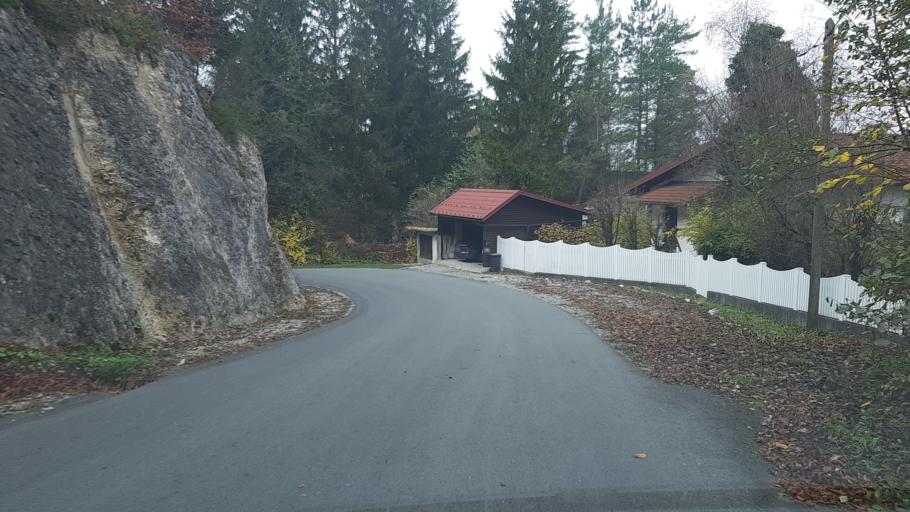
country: SI
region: Borovnica
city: Borovnica
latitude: 45.9118
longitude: 14.3660
